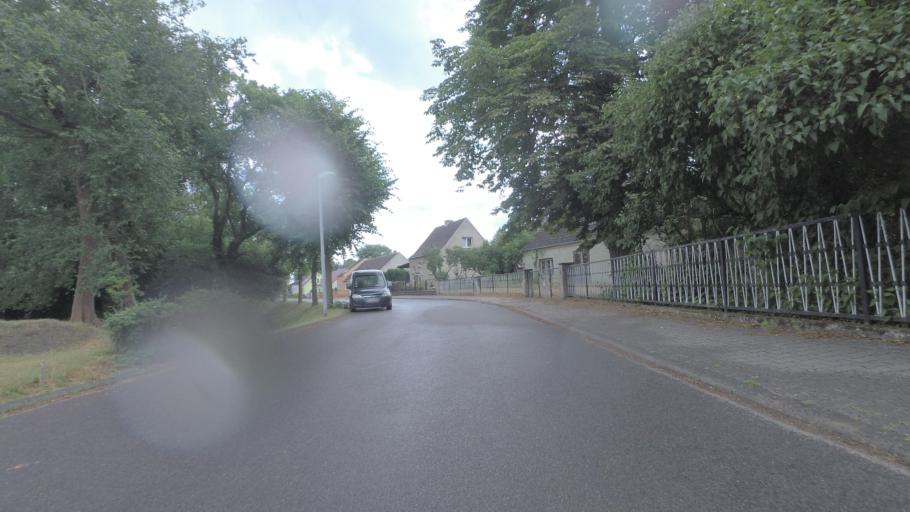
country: DE
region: Brandenburg
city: Sperenberg
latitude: 52.1395
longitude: 13.3635
